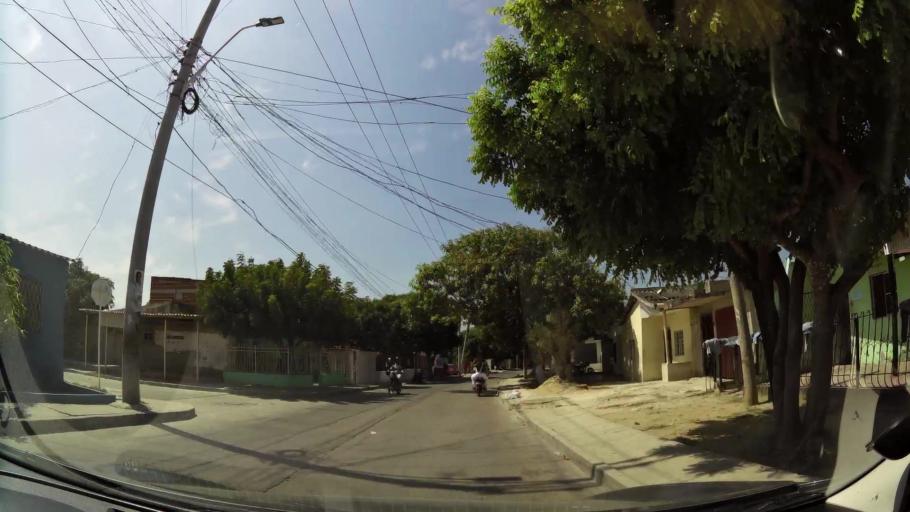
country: CO
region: Atlantico
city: Barranquilla
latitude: 10.9636
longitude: -74.8190
